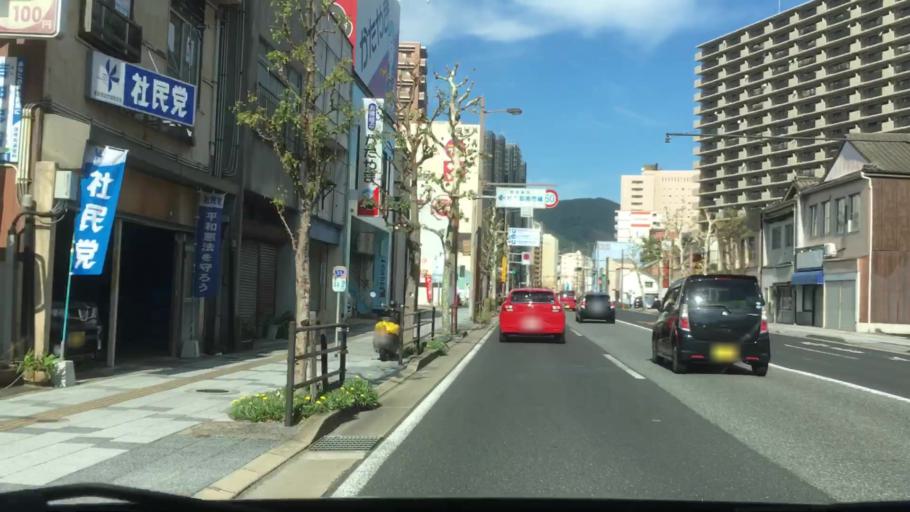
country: JP
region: Nagasaki
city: Sasebo
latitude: 33.1615
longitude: 129.7304
